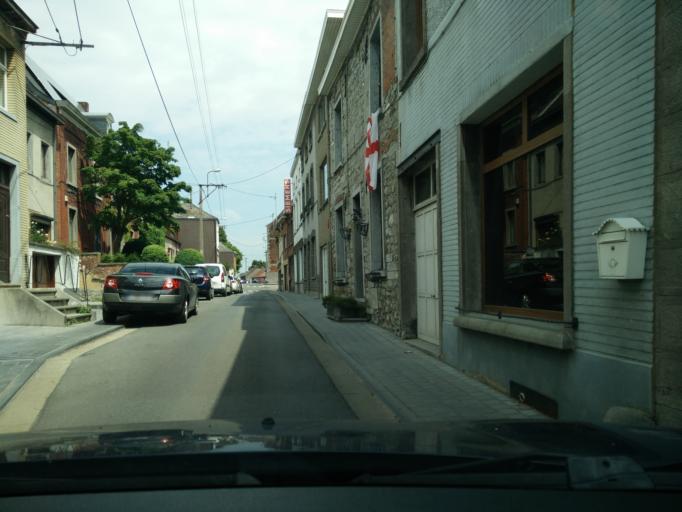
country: BE
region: Wallonia
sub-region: Province du Hainaut
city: Ecaussinnes-d'Enghien
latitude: 50.5709
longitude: 4.1762
